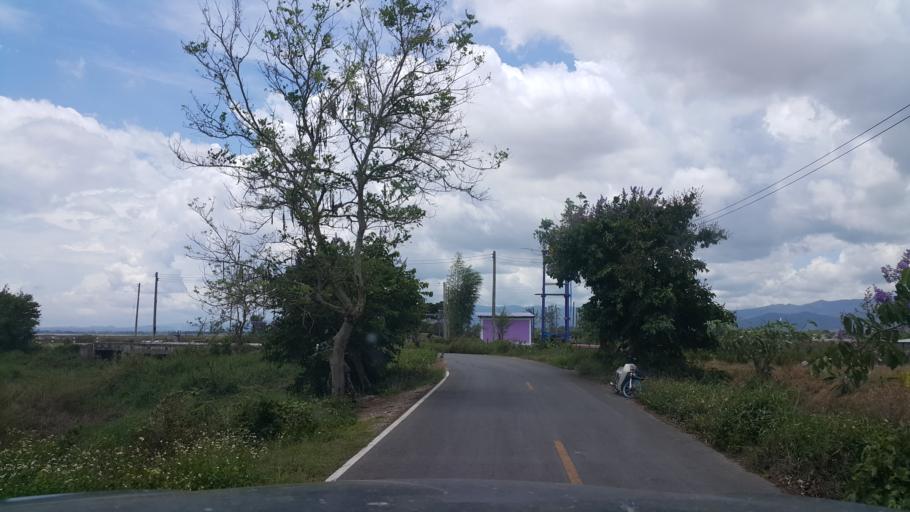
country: TH
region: Phayao
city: Phayao
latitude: 19.1882
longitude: 99.8560
